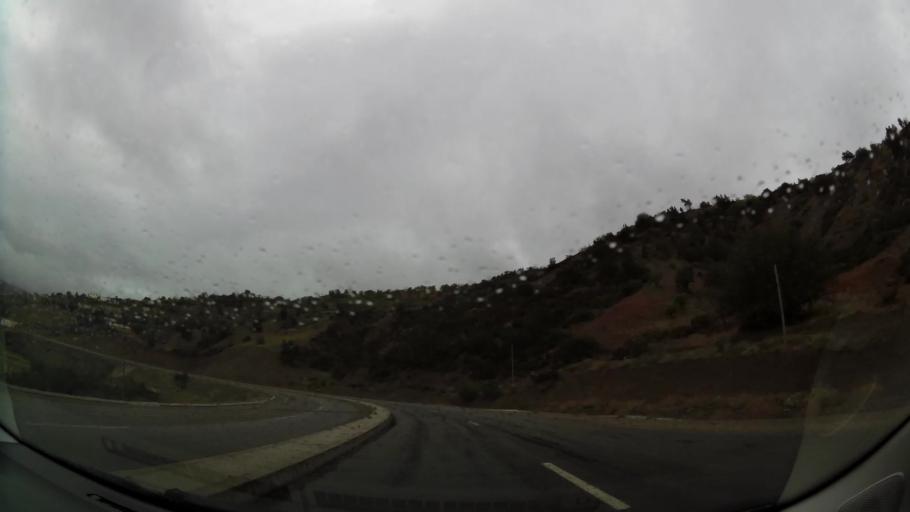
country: MA
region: Taza-Al Hoceima-Taounate
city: Imzourene
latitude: 34.9980
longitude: -3.8140
